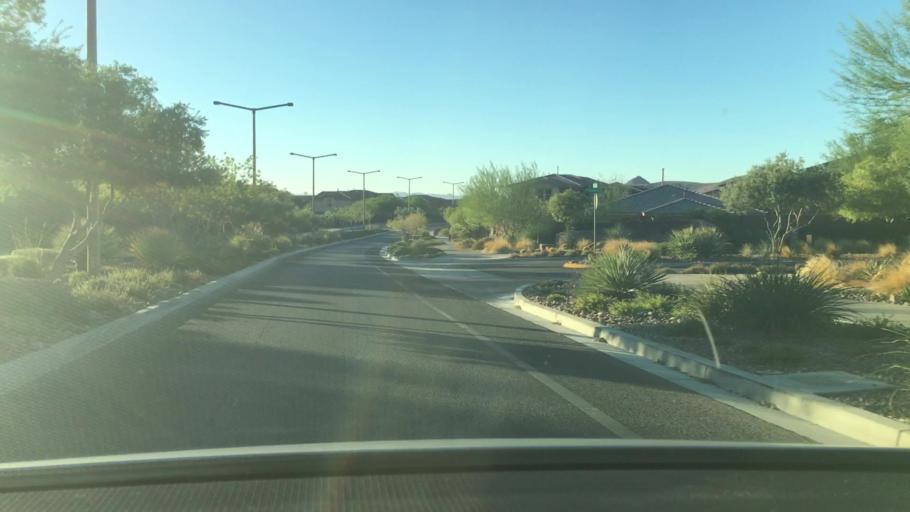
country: US
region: Nevada
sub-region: Clark County
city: Summerlin South
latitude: 36.0868
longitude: -115.3221
